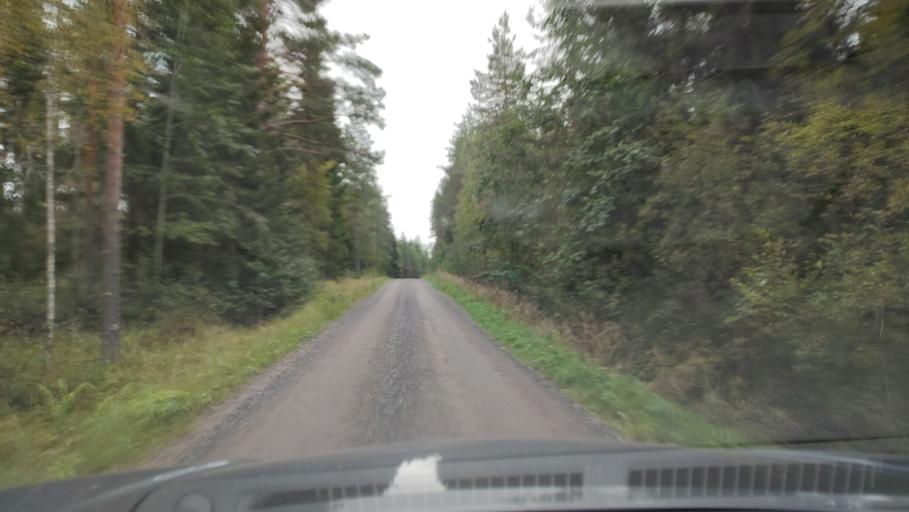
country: FI
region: Southern Ostrobothnia
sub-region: Suupohja
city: Karijoki
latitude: 62.2077
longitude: 21.5761
